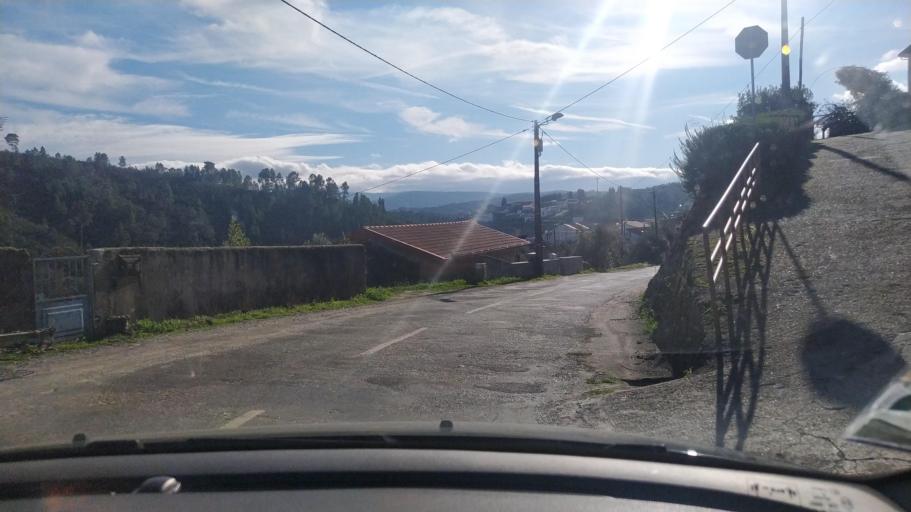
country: PT
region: Castelo Branco
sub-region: Concelho do Fundao
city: Aldeia de Joanes
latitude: 40.1812
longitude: -7.6949
